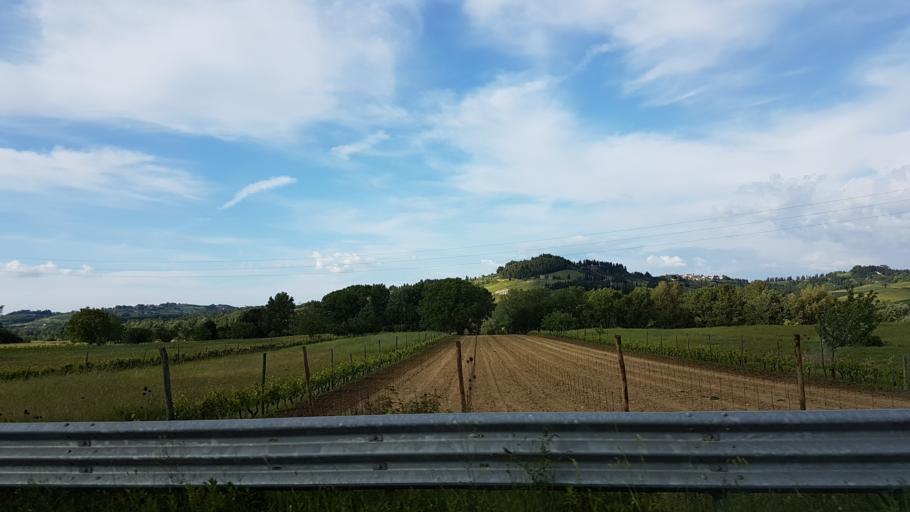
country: IT
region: Tuscany
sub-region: Province of Pisa
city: Lajatico
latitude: 43.4920
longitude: 10.7387
